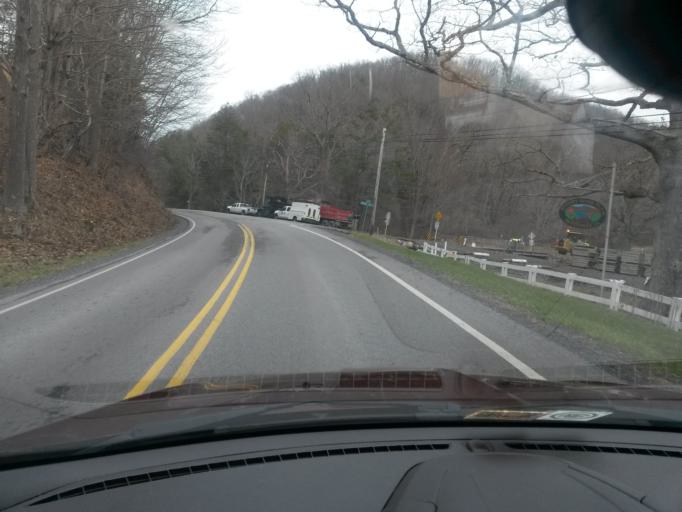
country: US
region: Virginia
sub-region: Highland County
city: Monterey
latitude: 38.3365
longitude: -79.6320
